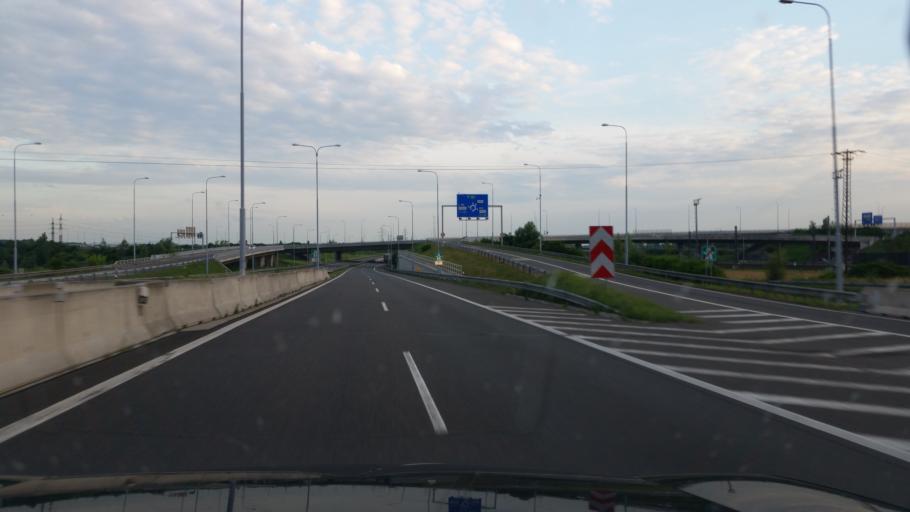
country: CZ
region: Moravskoslezsky
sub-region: Okres Ostrava-Mesto
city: Ostrava
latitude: 49.8134
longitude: 18.2078
